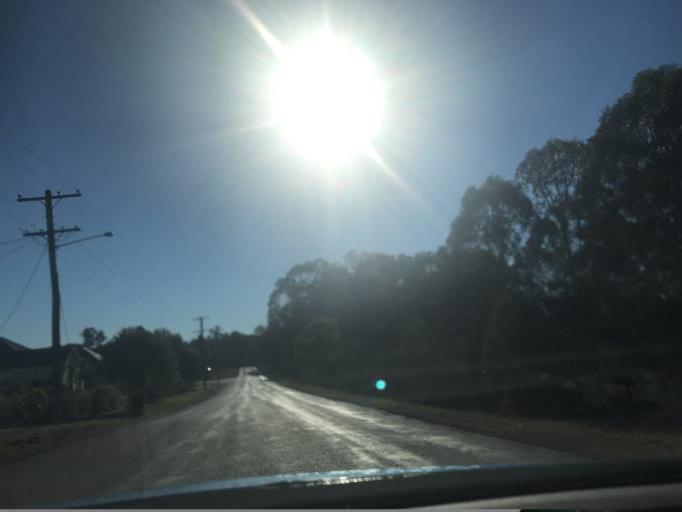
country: AU
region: New South Wales
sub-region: Cessnock
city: Cessnock
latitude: -32.9059
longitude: 151.2863
